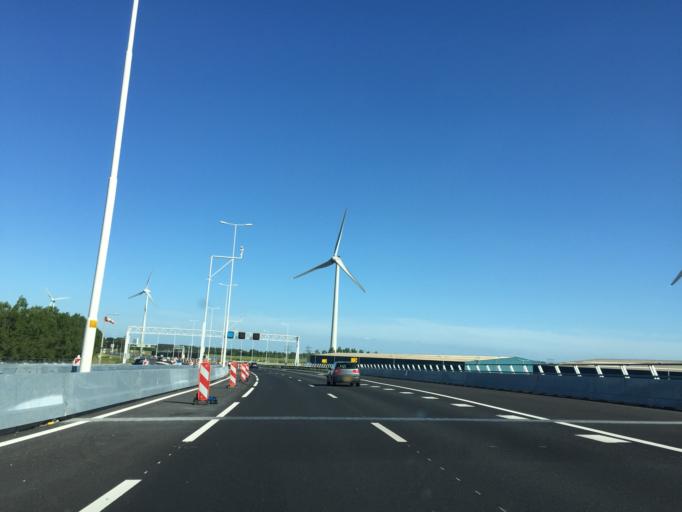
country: NL
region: South Holland
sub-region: Gemeente Maassluis
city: Maassluis
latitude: 51.8696
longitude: 4.2686
